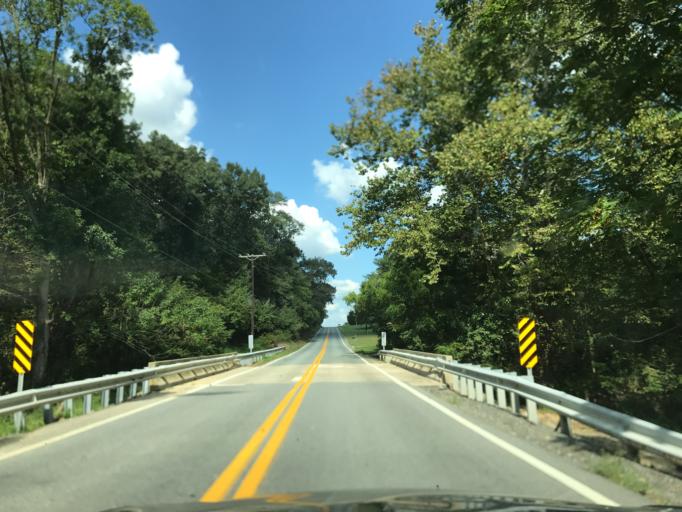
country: US
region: Delaware
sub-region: New Castle County
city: Townsend
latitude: 39.3773
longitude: -75.8019
